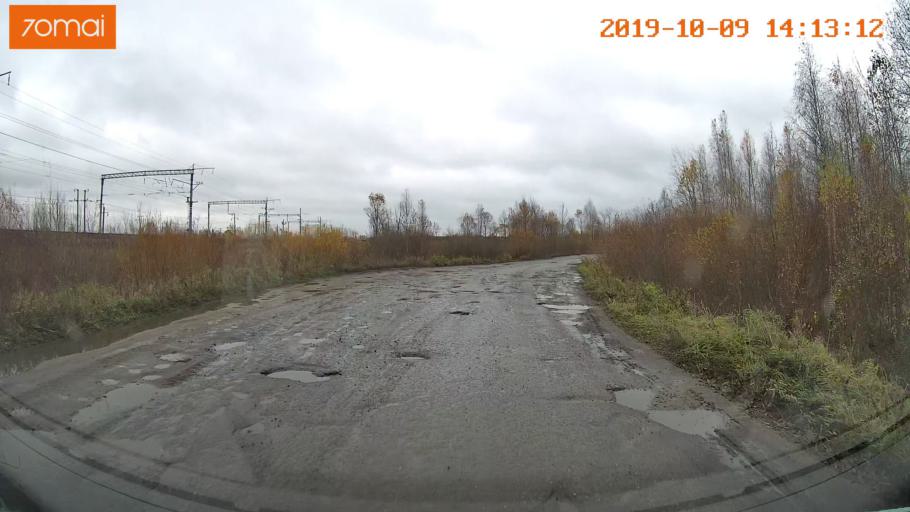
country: RU
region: Kostroma
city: Buy
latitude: 58.4819
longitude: 41.5113
